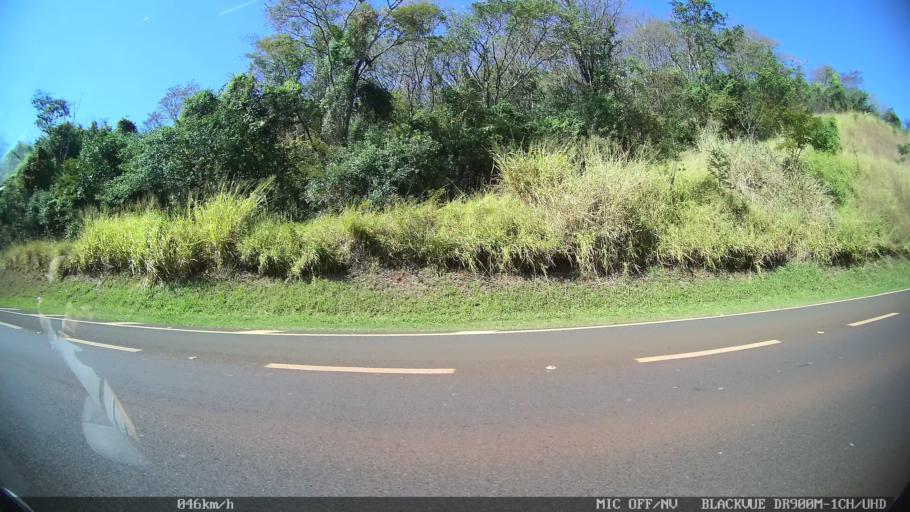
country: BR
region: Sao Paulo
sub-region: Franca
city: Franca
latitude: -20.6325
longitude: -47.4674
